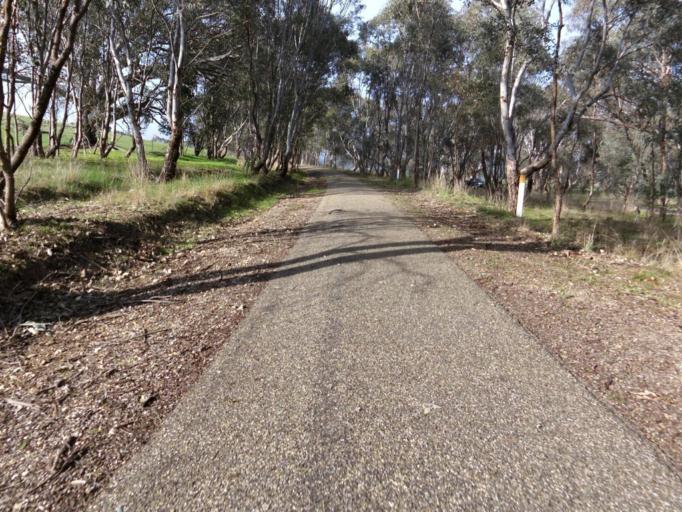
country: AU
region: Victoria
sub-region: Wangaratta
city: Wangaratta
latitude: -36.4477
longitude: 146.5513
